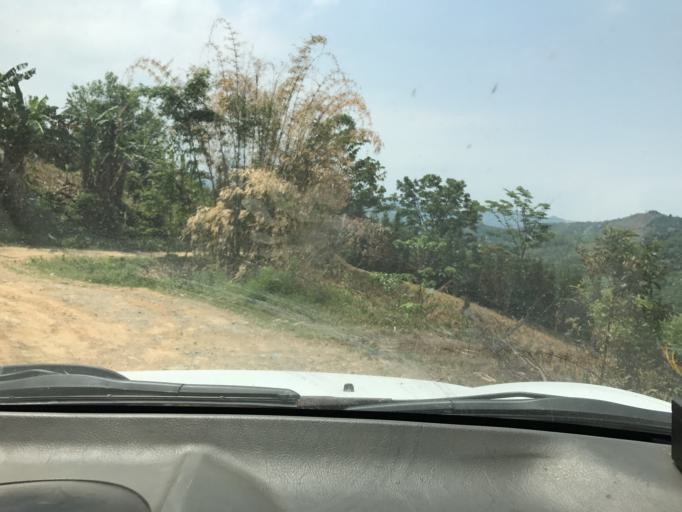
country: CN
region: Guangxi Zhuangzu Zizhiqu
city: Xinzhou
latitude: 24.9870
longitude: 105.9288
